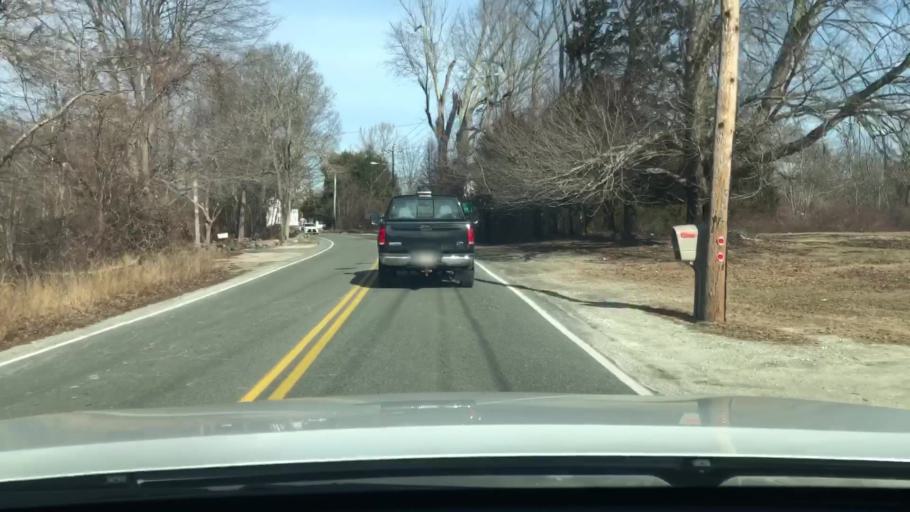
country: US
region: Massachusetts
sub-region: Worcester County
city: Blackstone
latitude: 42.0623
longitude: -71.5262
